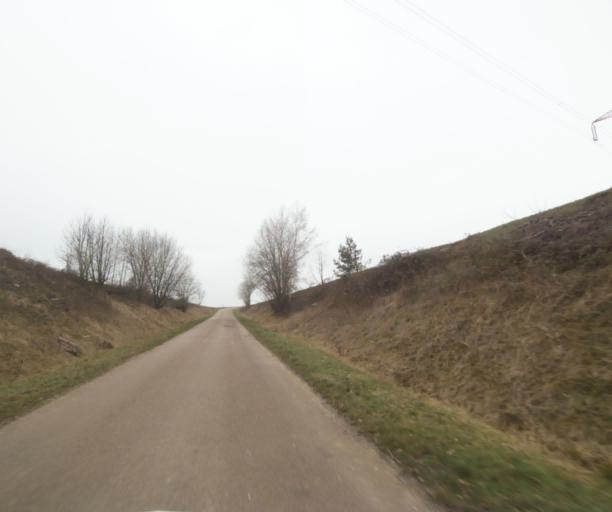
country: FR
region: Champagne-Ardenne
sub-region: Departement de la Haute-Marne
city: Chevillon
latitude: 48.5166
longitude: 5.0911
